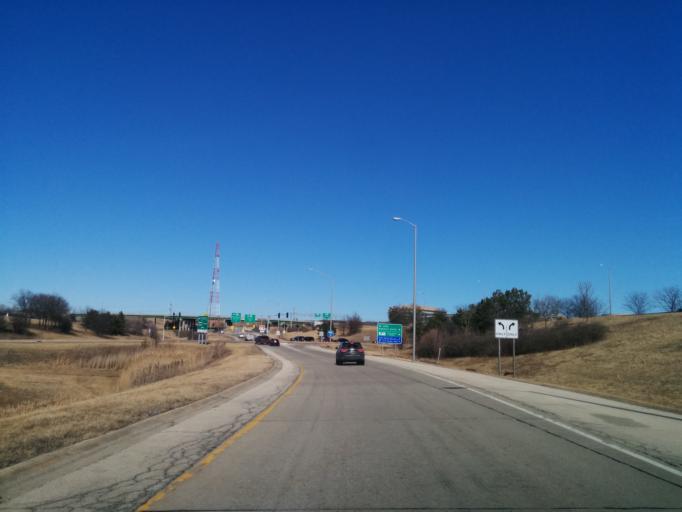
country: US
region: Illinois
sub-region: DuPage County
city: Lisle
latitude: 41.8024
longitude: -88.0551
